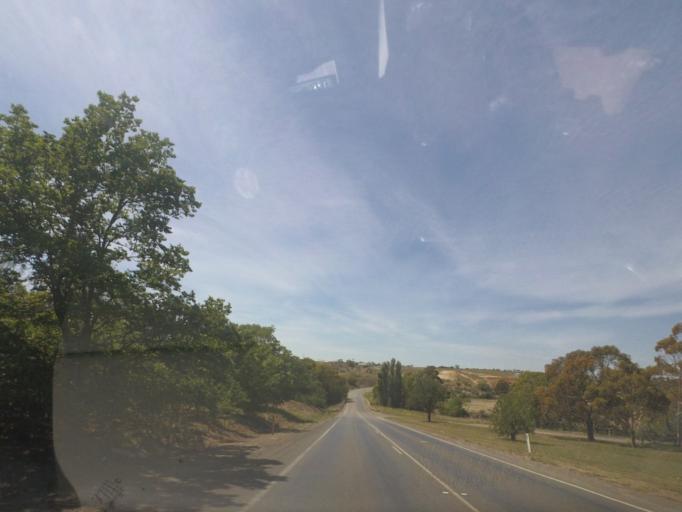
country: AU
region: Victoria
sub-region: Moorabool
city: Bacchus Marsh
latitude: -37.6961
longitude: 144.4474
